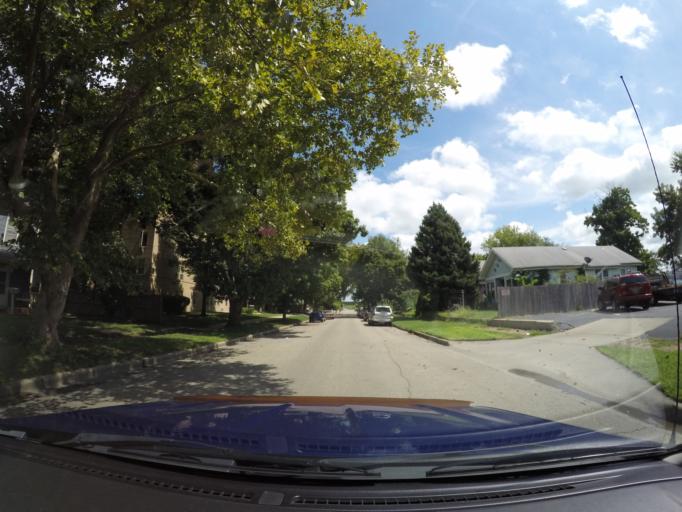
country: US
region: Kansas
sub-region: Riley County
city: Manhattan
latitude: 39.1762
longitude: -96.5632
